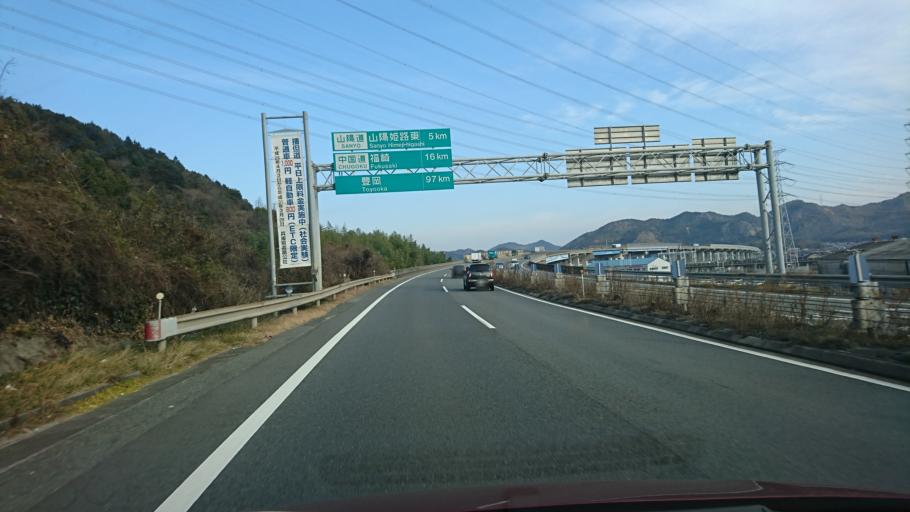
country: JP
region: Hyogo
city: Shirahamacho-usazakiminami
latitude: 34.8068
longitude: 134.7431
